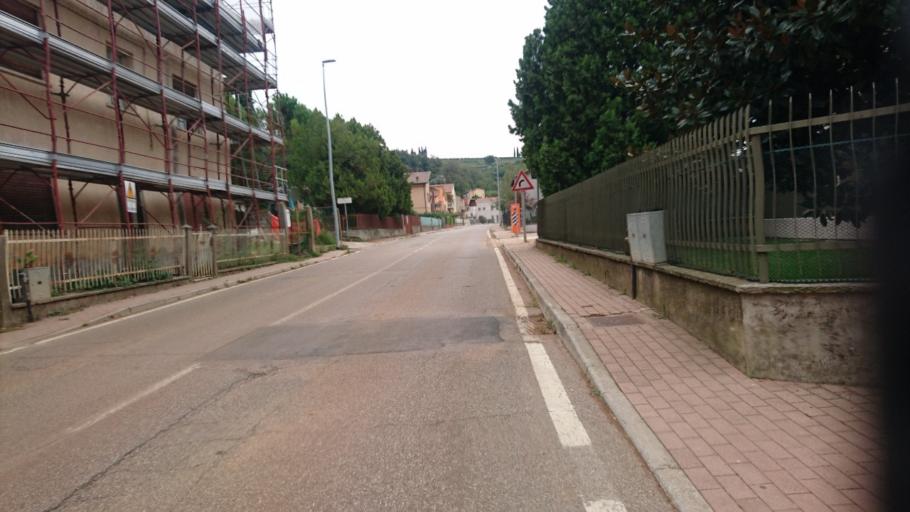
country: IT
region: Veneto
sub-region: Provincia di Verona
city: Soave
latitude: 45.4175
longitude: 11.2522
